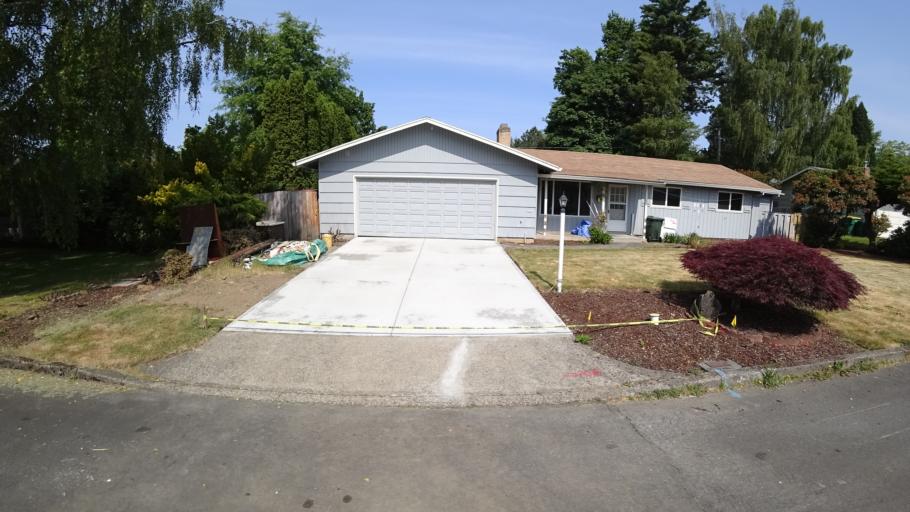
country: US
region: Oregon
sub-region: Washington County
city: Cedar Hills
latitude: 45.5050
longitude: -122.8196
